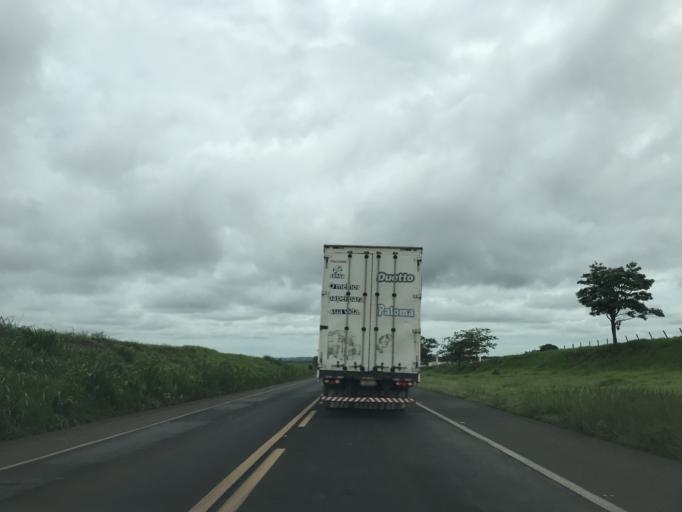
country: BR
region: Sao Paulo
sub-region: Nova Granada
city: Nova Granada
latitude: -20.4545
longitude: -49.2859
